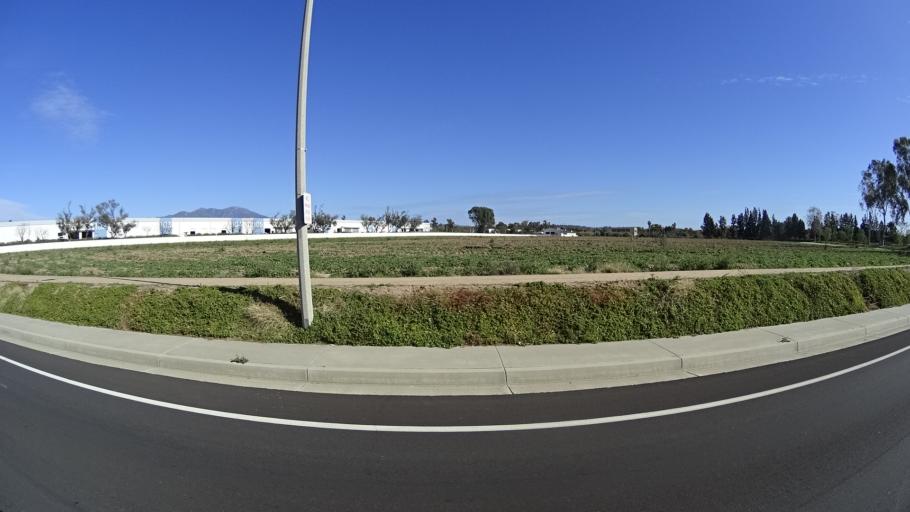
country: US
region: California
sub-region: Orange County
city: Lake Forest
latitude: 33.6581
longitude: -117.7106
